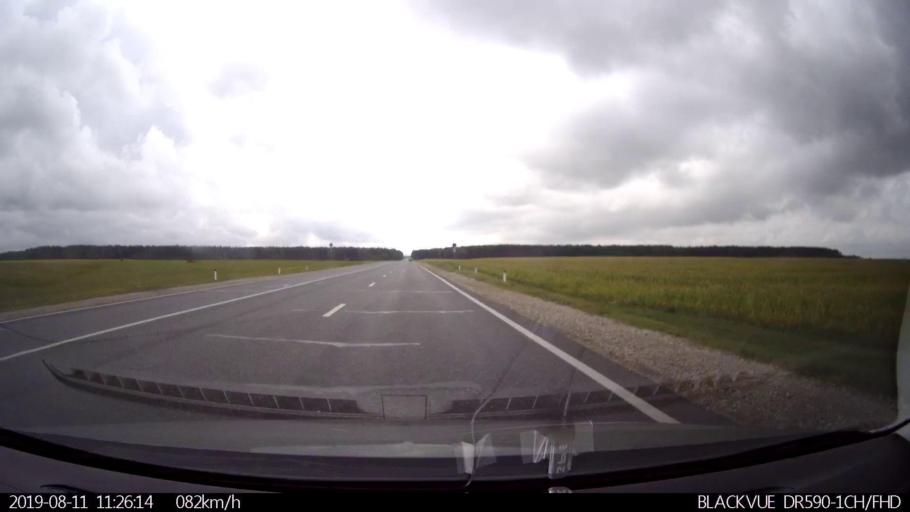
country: RU
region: Ulyanovsk
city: Krasnyy Gulyay
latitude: 54.1079
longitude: 48.2358
